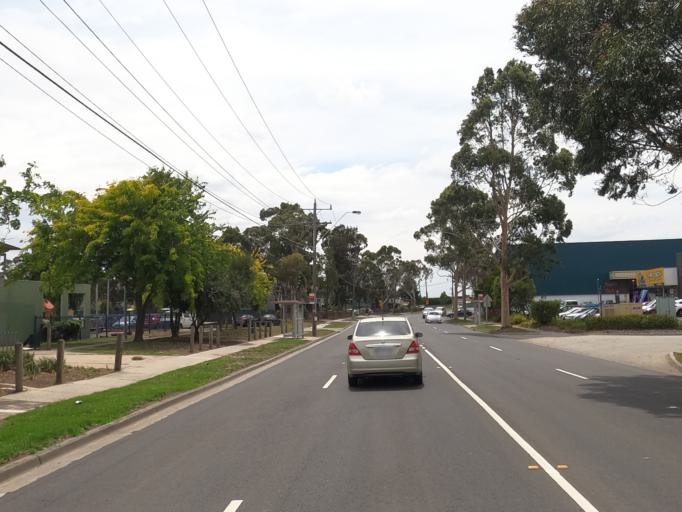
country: AU
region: Victoria
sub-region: Hume
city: Broadmeadows
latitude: -37.6766
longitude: 144.9195
